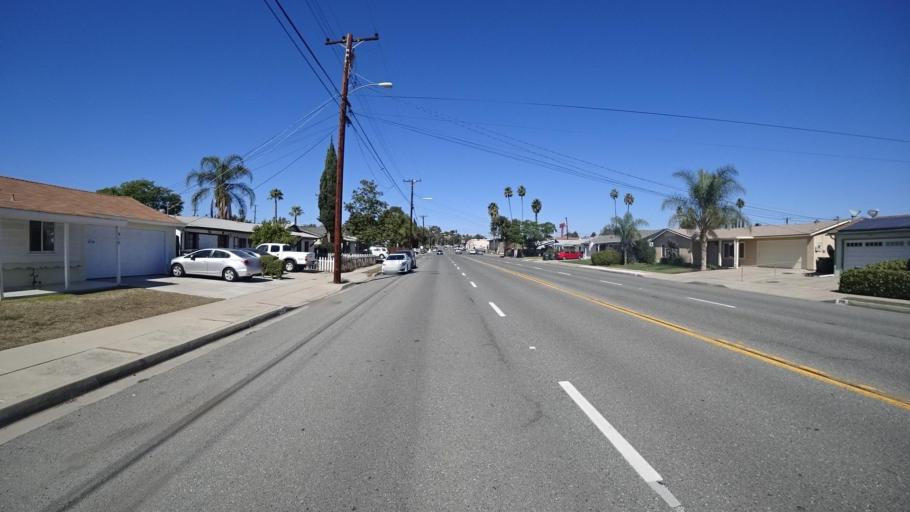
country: US
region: California
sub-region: San Diego County
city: La Presa
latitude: 32.7114
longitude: -117.0161
